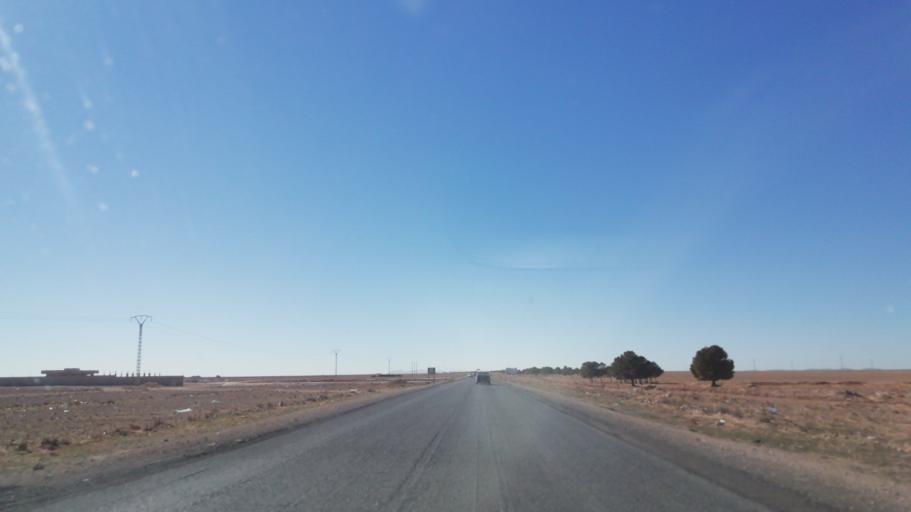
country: DZ
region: Saida
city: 'Ain el Hadjar
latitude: 34.0171
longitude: 0.0603
